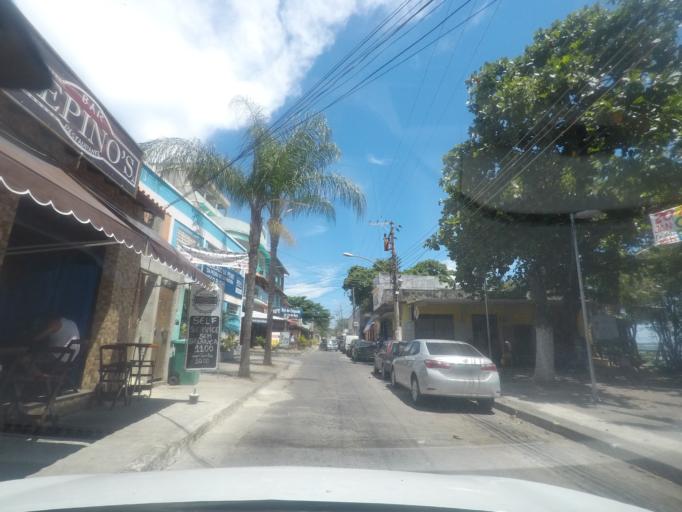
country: BR
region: Rio de Janeiro
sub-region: Itaguai
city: Itaguai
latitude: -23.0016
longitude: -43.6421
